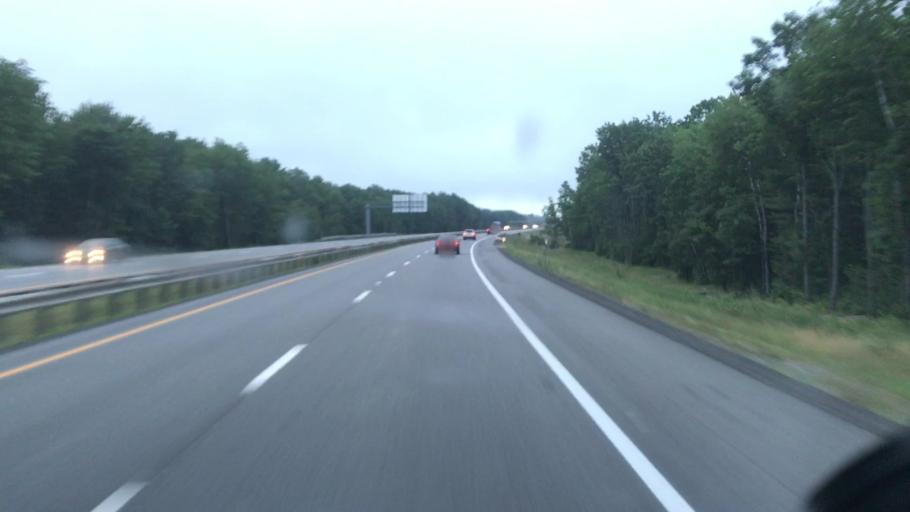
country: US
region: Maine
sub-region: Cumberland County
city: New Gloucester
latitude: 43.9505
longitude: -70.3322
